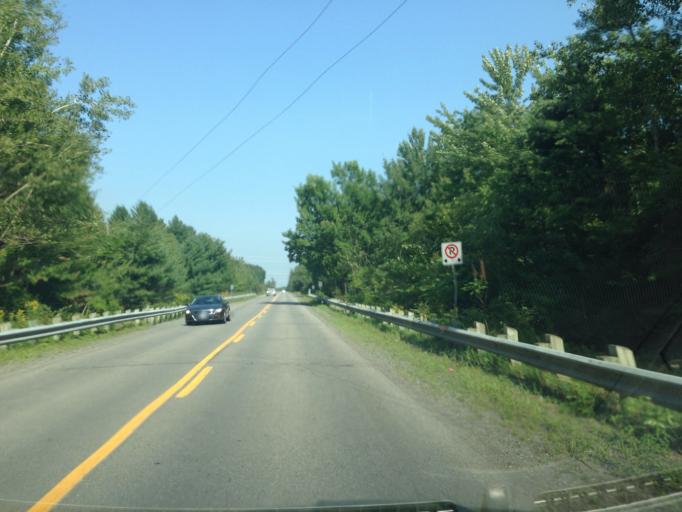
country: CA
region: Ontario
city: Ottawa
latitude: 45.4033
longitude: -75.5578
